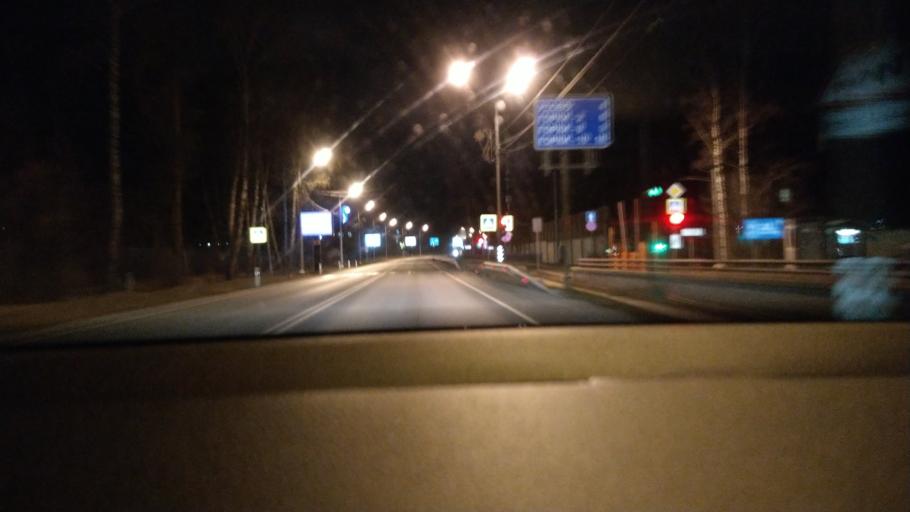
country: RU
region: Moskovskaya
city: Barvikha
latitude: 55.7381
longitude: 37.2590
